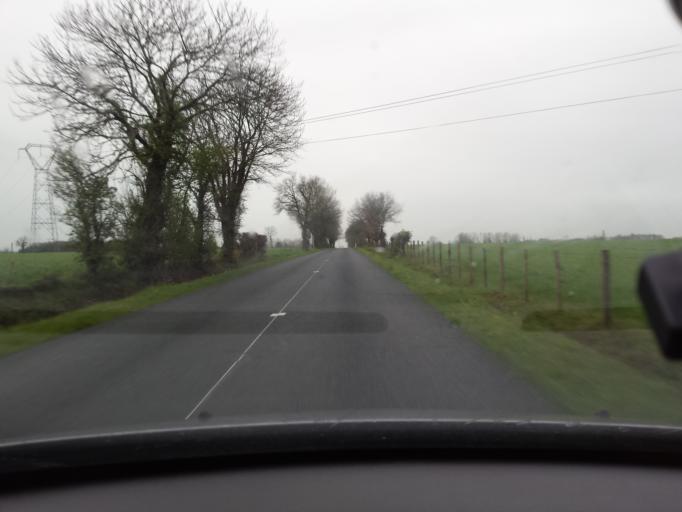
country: FR
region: Pays de la Loire
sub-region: Departement de la Vendee
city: La Ferriere
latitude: 46.7475
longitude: -1.3090
